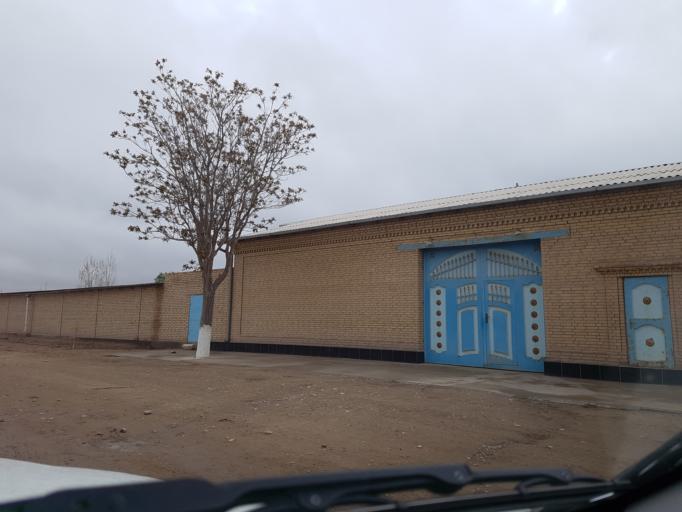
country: TM
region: Lebap
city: Sayat
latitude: 38.4544
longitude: 64.3673
